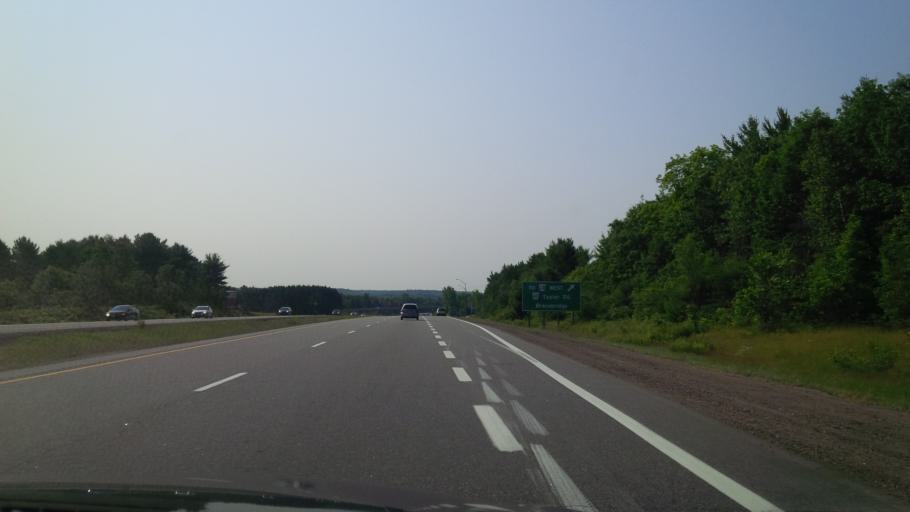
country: CA
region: Ontario
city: Bracebridge
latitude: 45.0580
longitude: -79.2938
